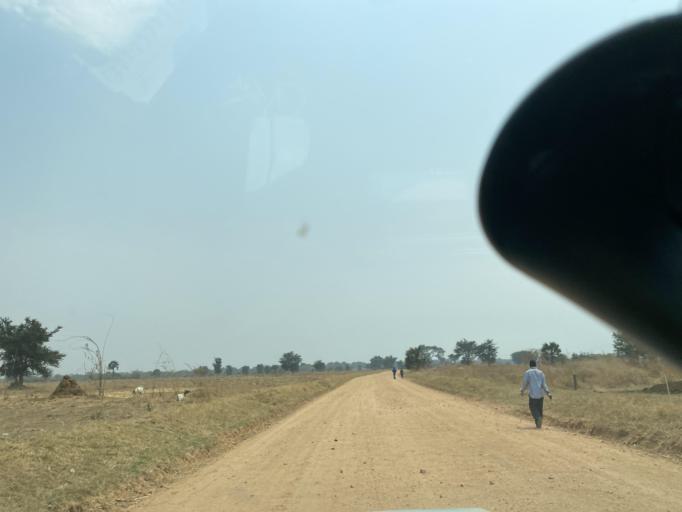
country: ZM
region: Lusaka
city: Kafue
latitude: -15.6362
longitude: 28.0983
